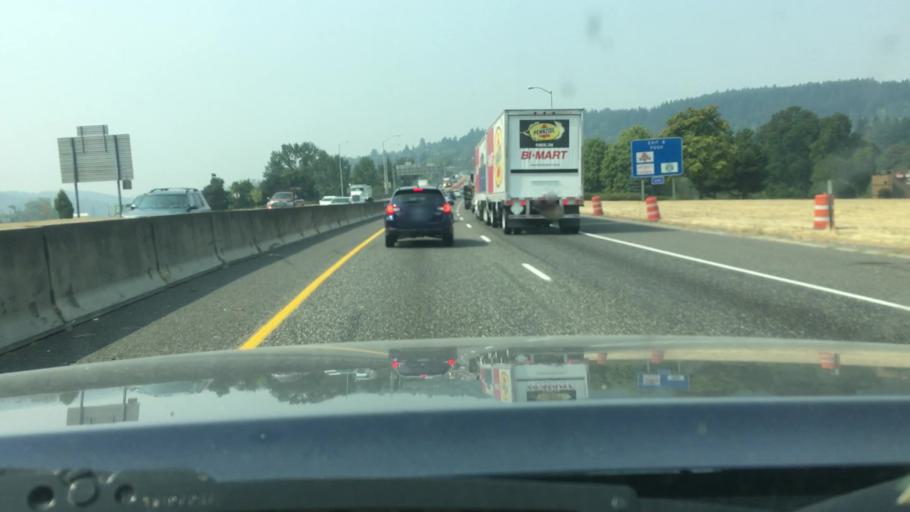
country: US
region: Oregon
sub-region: Clackamas County
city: Oregon City
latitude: 45.3663
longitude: -122.5980
